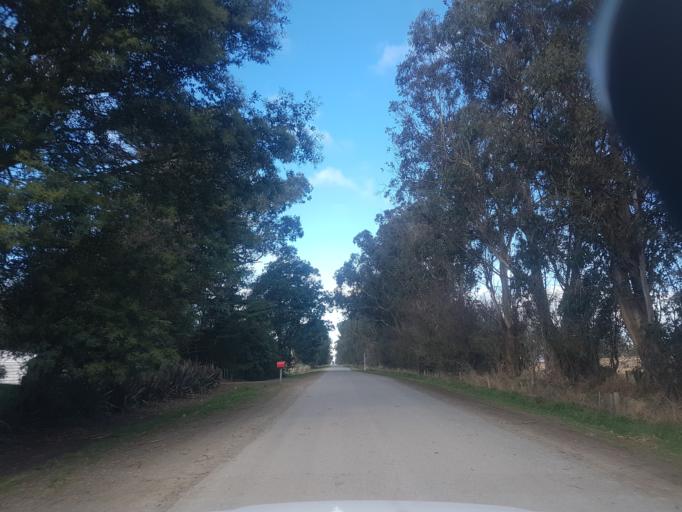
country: NZ
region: Canterbury
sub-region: Timaru District
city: Pleasant Point
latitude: -44.2079
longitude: 171.2083
